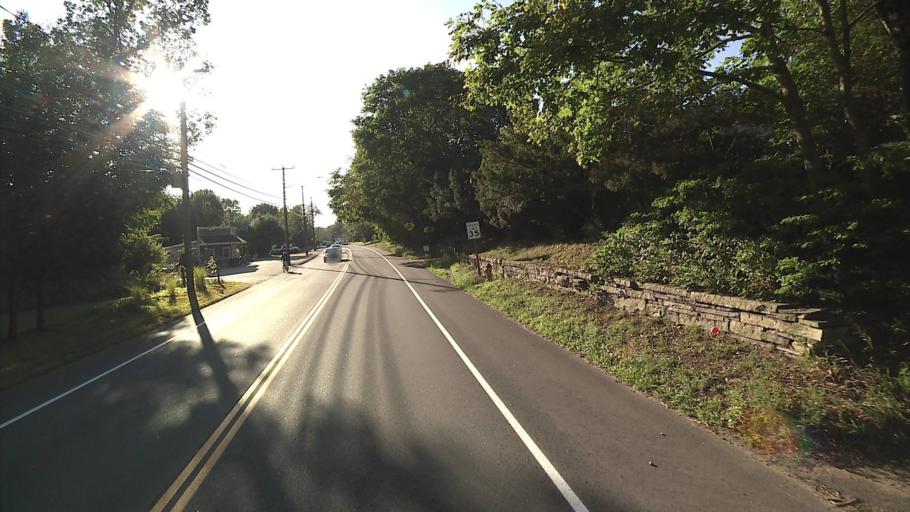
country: US
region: Connecticut
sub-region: Windham County
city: Willimantic
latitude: 41.7052
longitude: -72.1964
